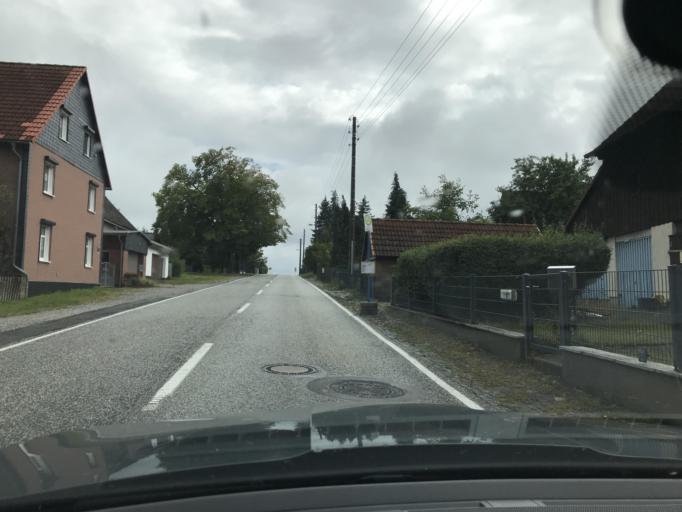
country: DE
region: Saxony-Anhalt
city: Huttenrode
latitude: 51.7668
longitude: 10.9035
